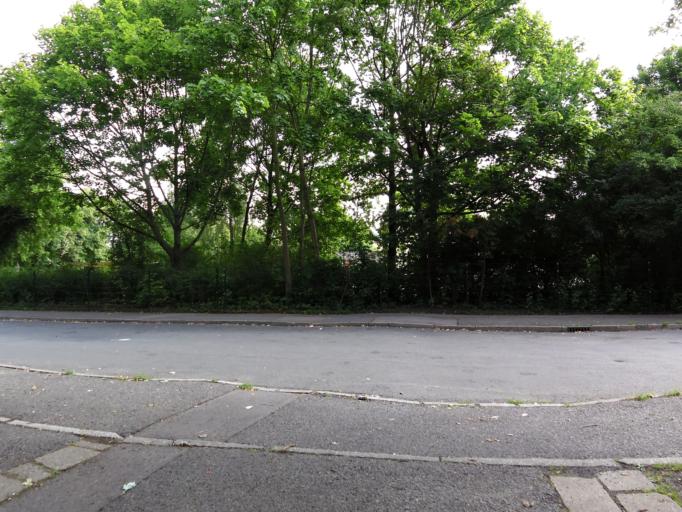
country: DE
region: Saxony
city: Leipzig
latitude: 51.3770
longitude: 12.4181
